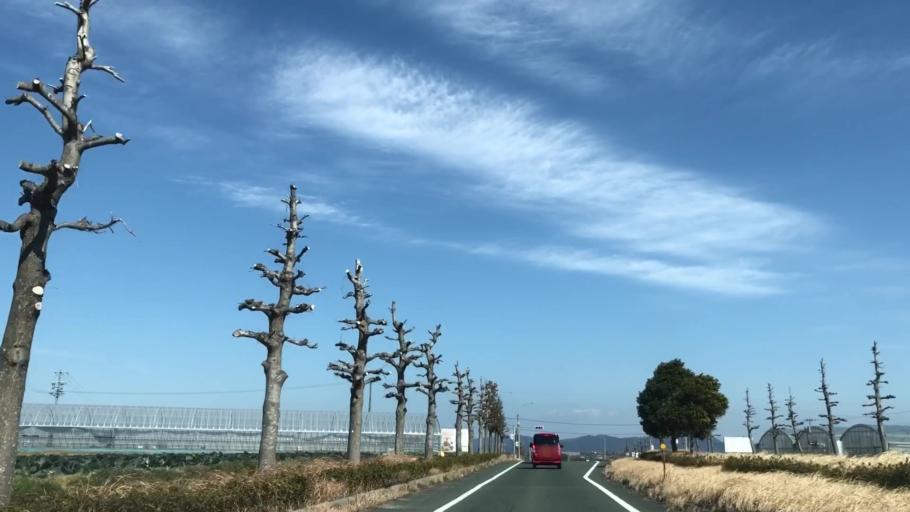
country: JP
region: Aichi
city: Toyohashi
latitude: 34.7095
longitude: 137.3558
